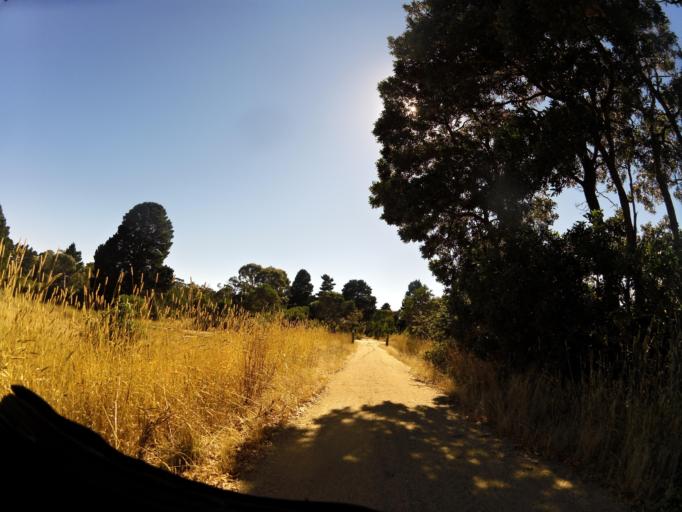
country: AU
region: Victoria
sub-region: Ballarat North
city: Delacombe
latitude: -37.6824
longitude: 143.4266
